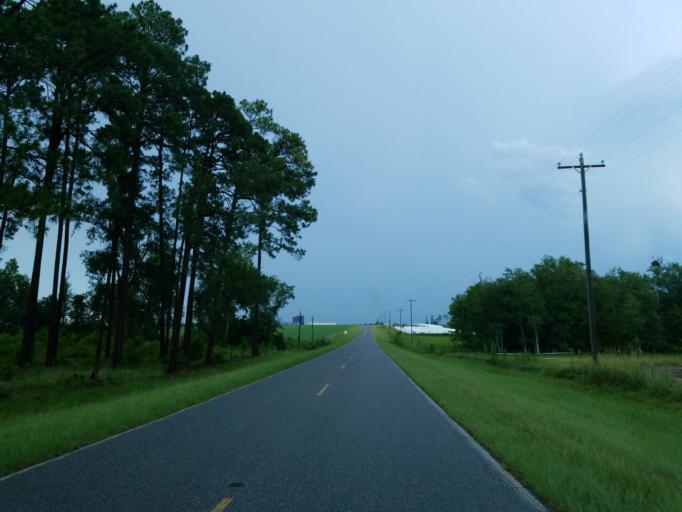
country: US
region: Georgia
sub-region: Cook County
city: Adel
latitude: 31.0751
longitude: -83.4360
